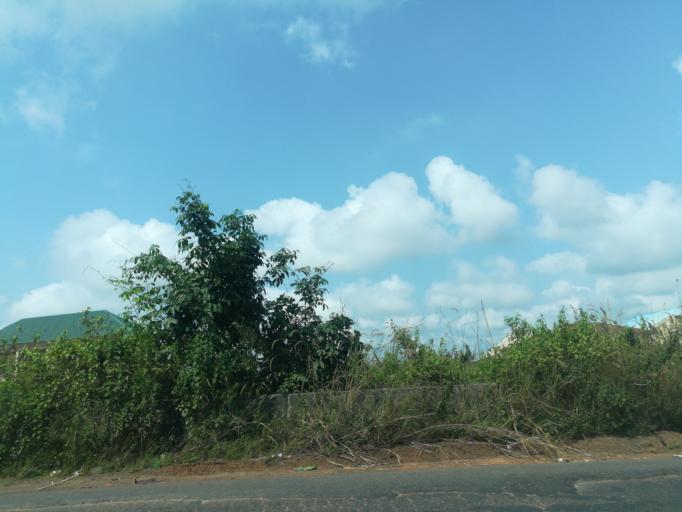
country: NG
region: Oyo
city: Moniya
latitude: 7.5328
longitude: 3.9166
